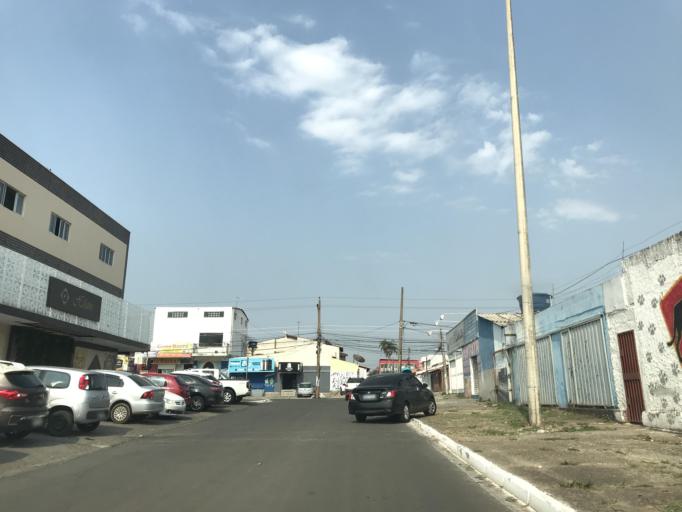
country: BR
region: Federal District
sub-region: Brasilia
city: Brasilia
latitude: -15.8154
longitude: -48.0827
